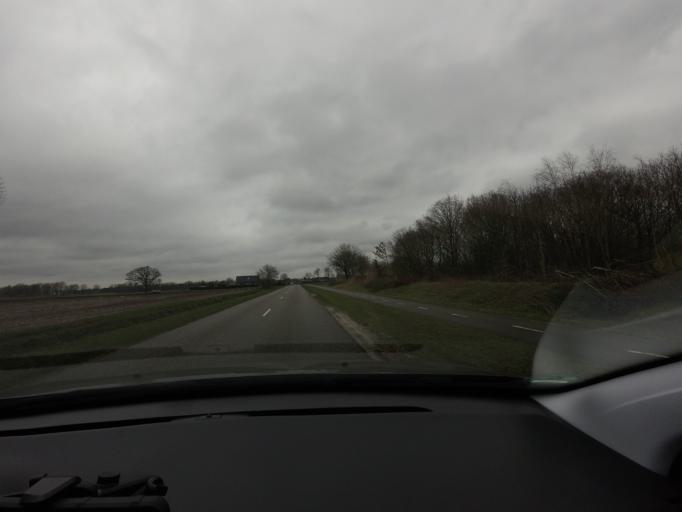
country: NL
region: Drenthe
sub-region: Gemeente Hoogeveen
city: Hoogeveen
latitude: 52.8390
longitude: 6.5332
